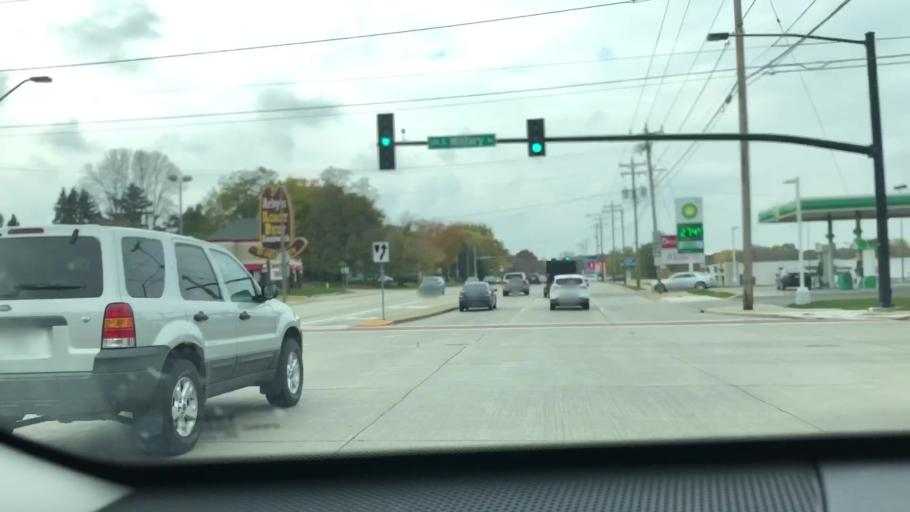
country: US
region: Wisconsin
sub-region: Brown County
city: Howard
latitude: 44.5237
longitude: -88.0640
